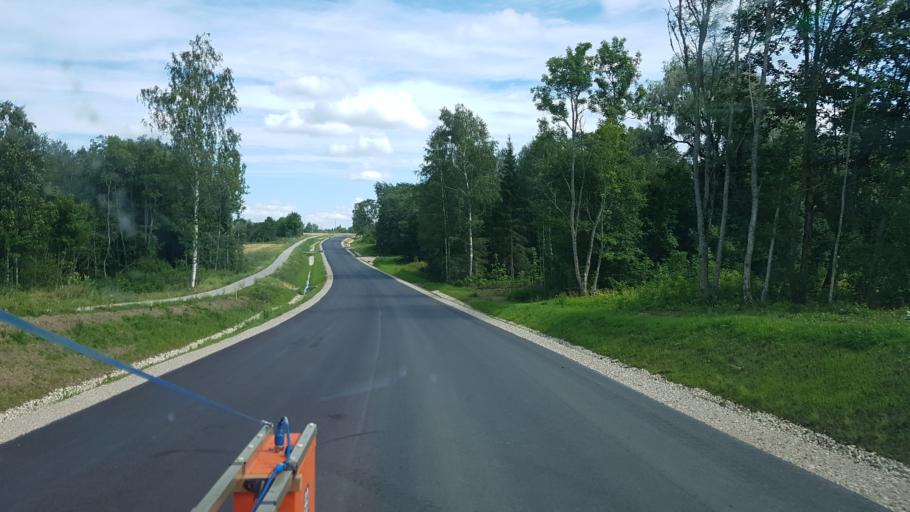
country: EE
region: Viljandimaa
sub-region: Suure-Jaani vald
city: Suure-Jaani
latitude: 58.5402
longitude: 25.5228
